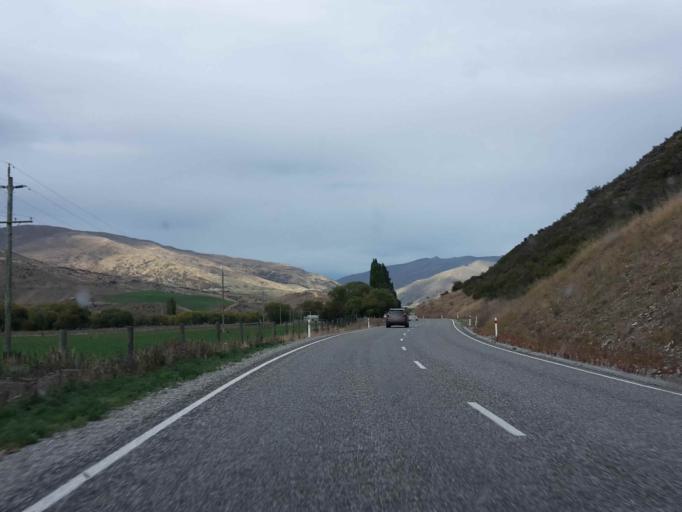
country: NZ
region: Otago
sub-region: Queenstown-Lakes District
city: Wanaka
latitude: -44.8448
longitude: 169.0468
